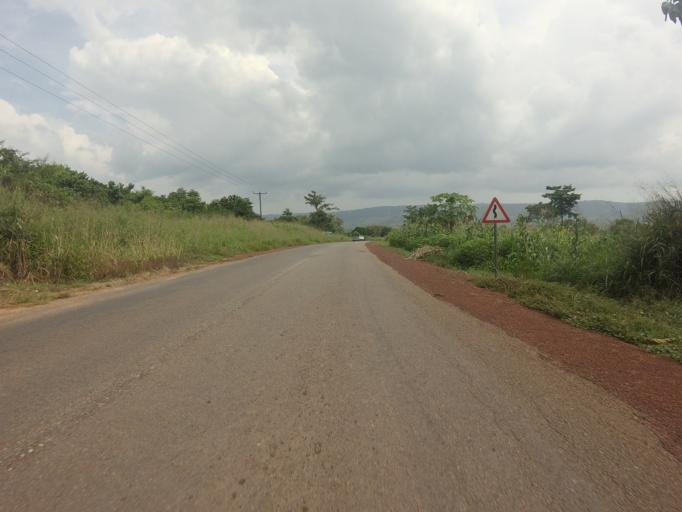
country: GH
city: Akropong
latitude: 5.9556
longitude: -0.1813
